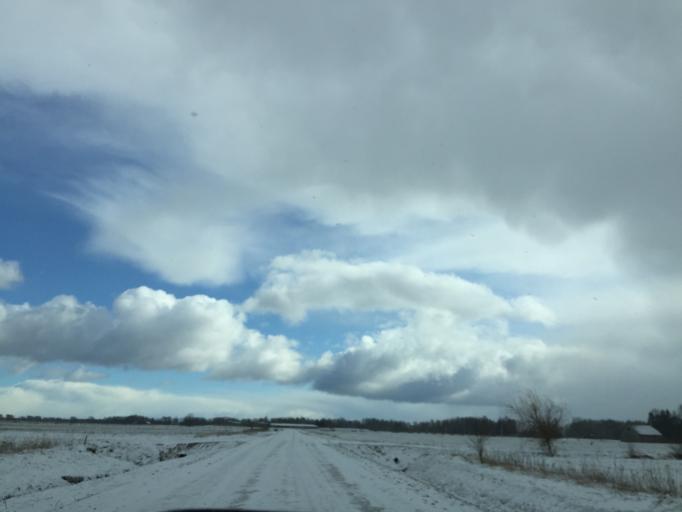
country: LV
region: Ventspils
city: Ventspils
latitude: 57.3742
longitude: 21.6213
